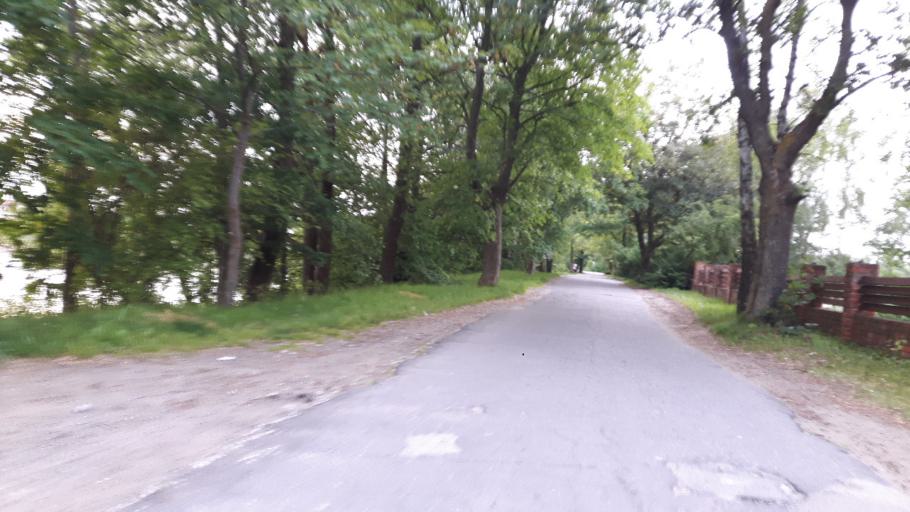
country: RU
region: Kaliningrad
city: Vzmorye
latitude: 54.6475
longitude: 20.3569
